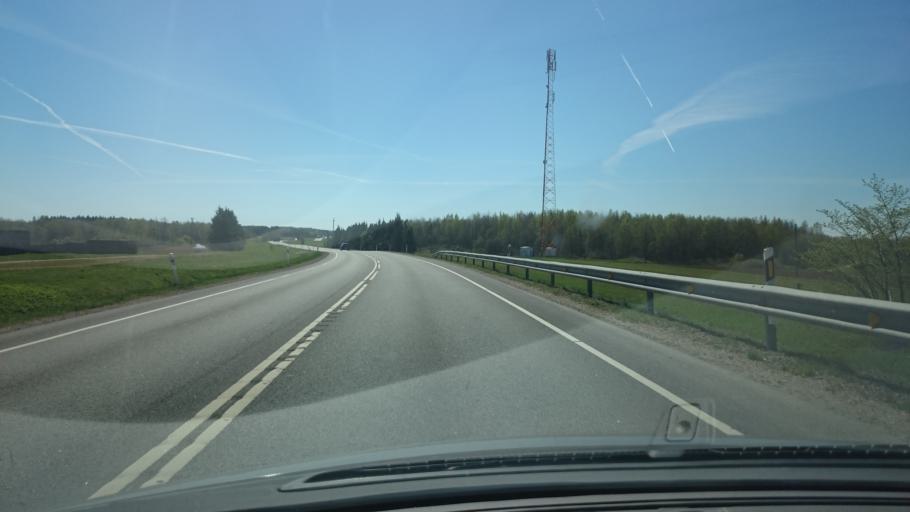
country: EE
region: Ida-Virumaa
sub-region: Narva-Joesuu linn
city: Narva-Joesuu
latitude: 59.3893
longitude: 27.9787
